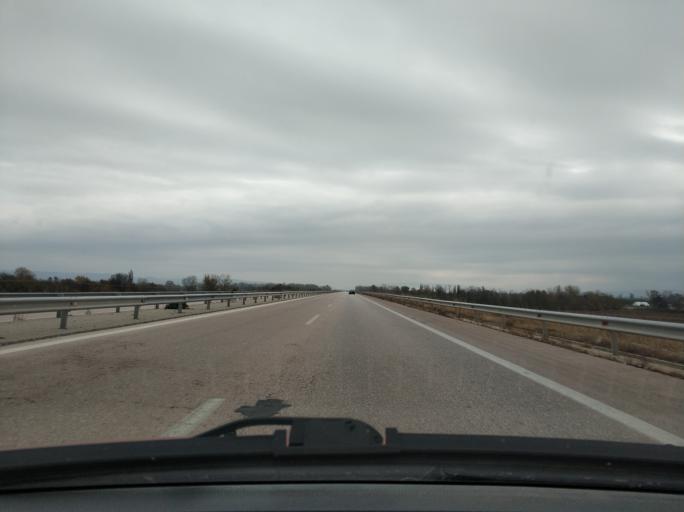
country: GR
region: Central Macedonia
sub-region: Nomos Thessalonikis
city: Kavallari
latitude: 40.7337
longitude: 23.0434
